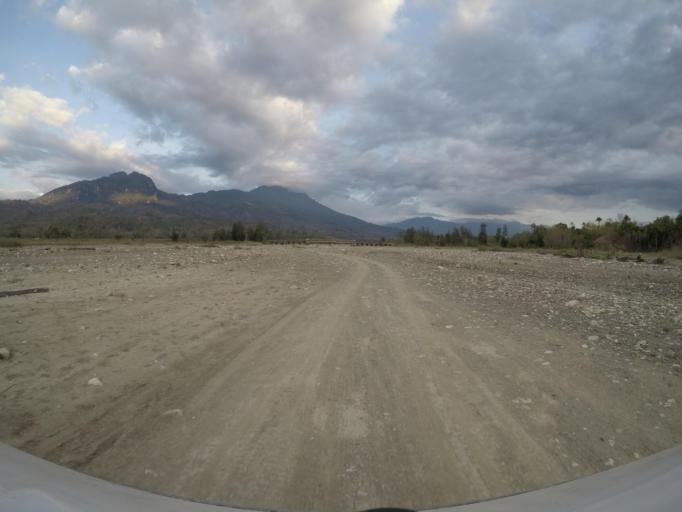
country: TL
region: Bobonaro
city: Maliana
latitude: -8.9093
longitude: 125.2132
